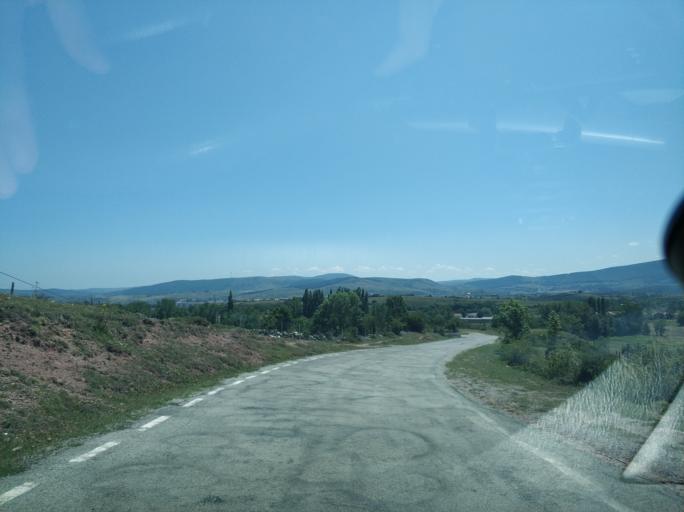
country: ES
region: Cantabria
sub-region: Provincia de Cantabria
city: Reinosa
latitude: 43.0223
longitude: -4.1662
